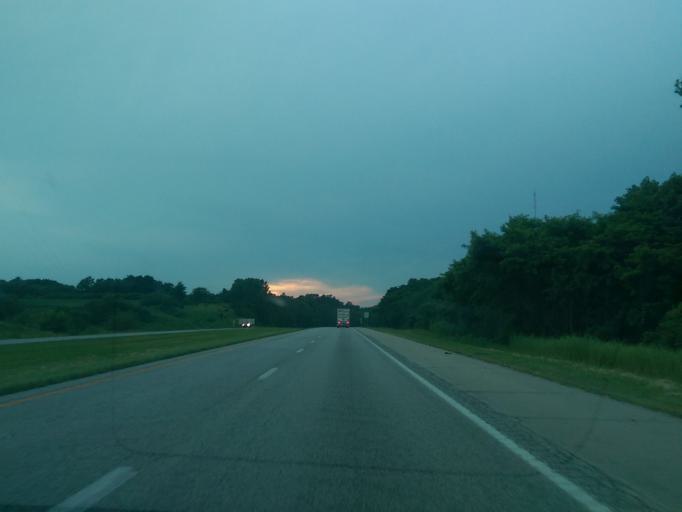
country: US
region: Missouri
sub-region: Holt County
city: Mound City
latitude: 40.0775
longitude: -95.2009
